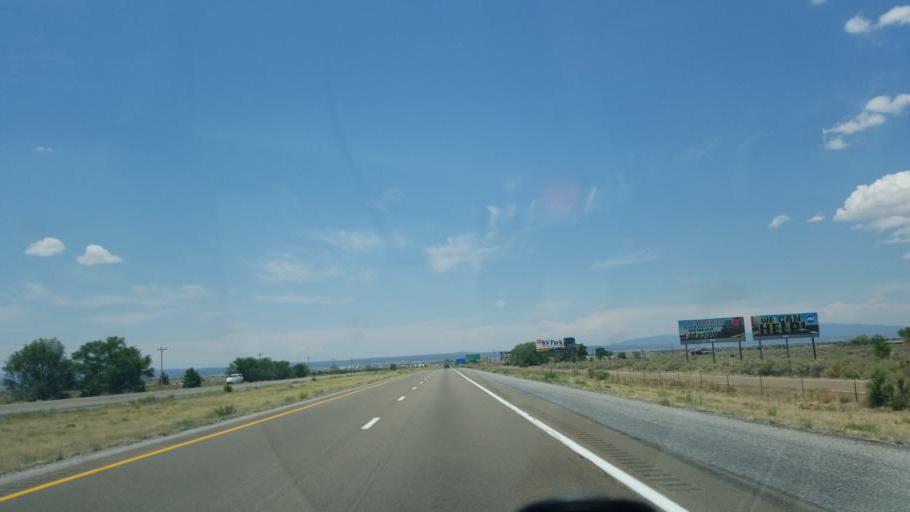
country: US
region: New Mexico
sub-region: Torrance County
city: Moriarty
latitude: 35.0049
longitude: -105.9739
